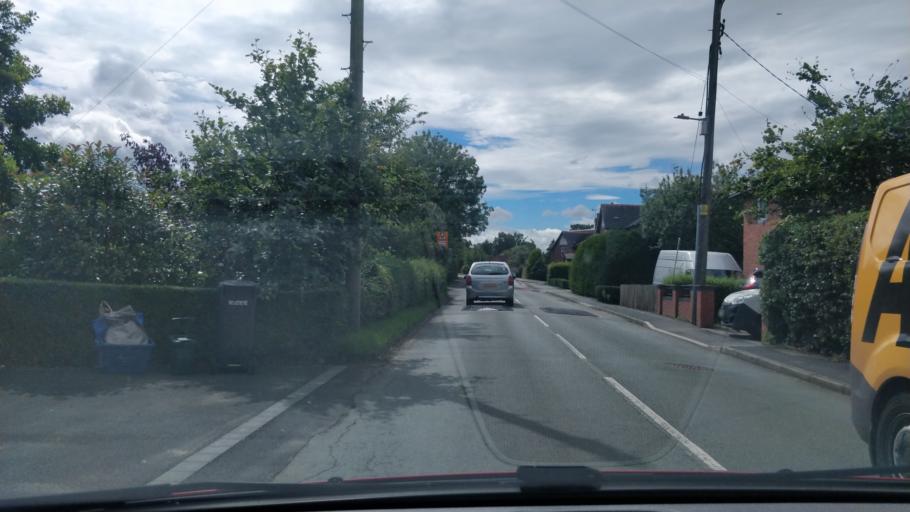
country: GB
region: Wales
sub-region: County of Flintshire
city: Hope
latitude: 53.1469
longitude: -3.0008
